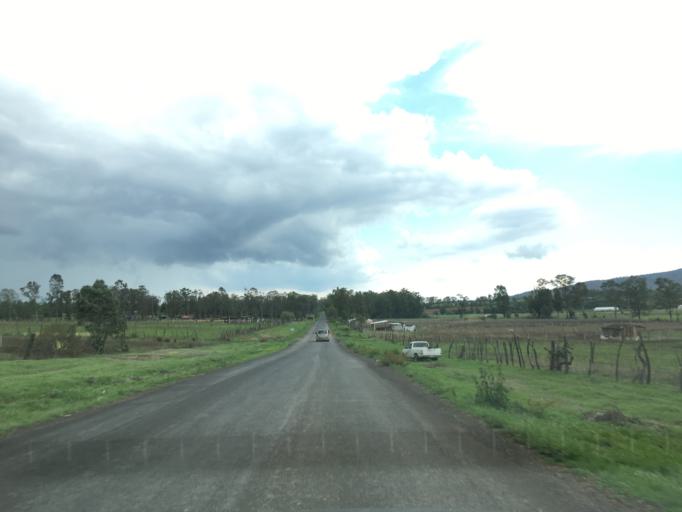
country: MX
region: Michoacan
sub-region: Morelia
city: La Mintzita (Piedra Dura)
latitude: 19.5663
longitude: -101.2747
